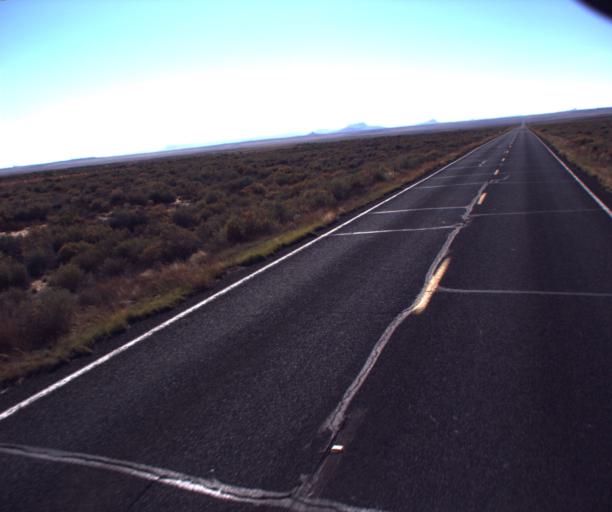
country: US
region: Arizona
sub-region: Navajo County
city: First Mesa
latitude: 35.7222
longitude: -110.5155
